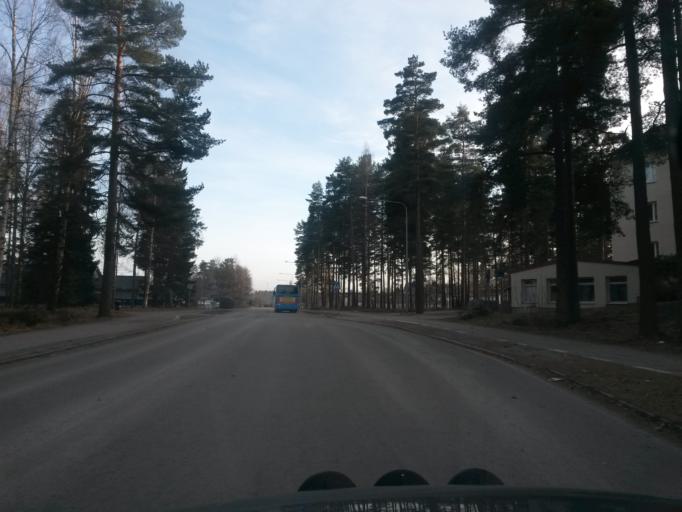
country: SE
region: OErebro
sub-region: Karlskoga Kommun
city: Karlskoga
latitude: 59.3173
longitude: 14.4953
